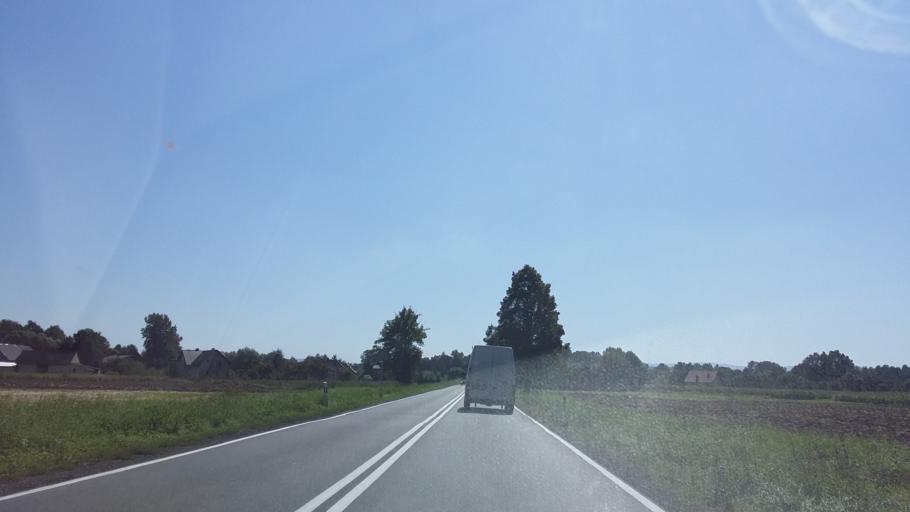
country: PL
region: Lesser Poland Voivodeship
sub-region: Powiat oswiecimski
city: Zator
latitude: 49.9656
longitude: 19.4409
